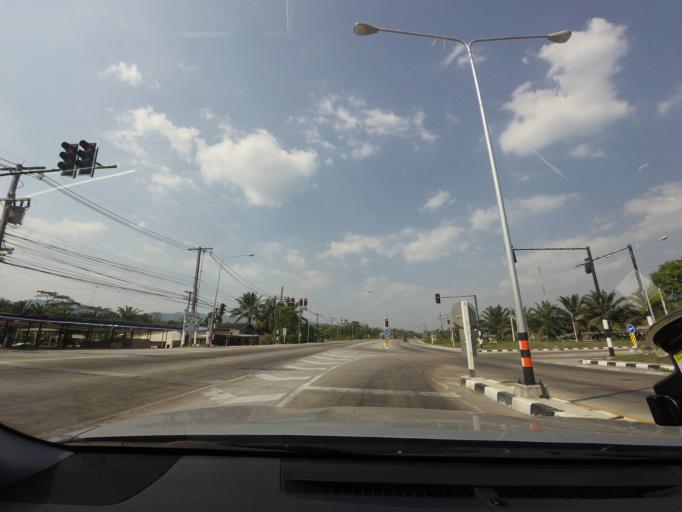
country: TH
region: Phangnga
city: Thap Put
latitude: 8.5775
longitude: 98.7407
